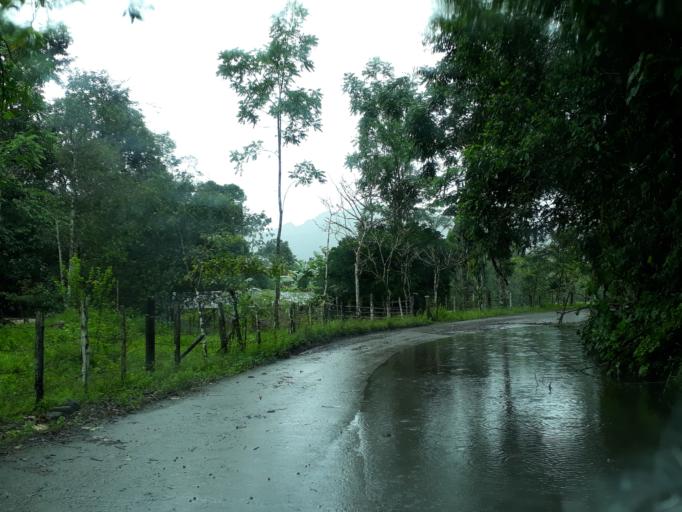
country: CO
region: Boyaca
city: Santa Maria
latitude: 4.7270
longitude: -73.2959
